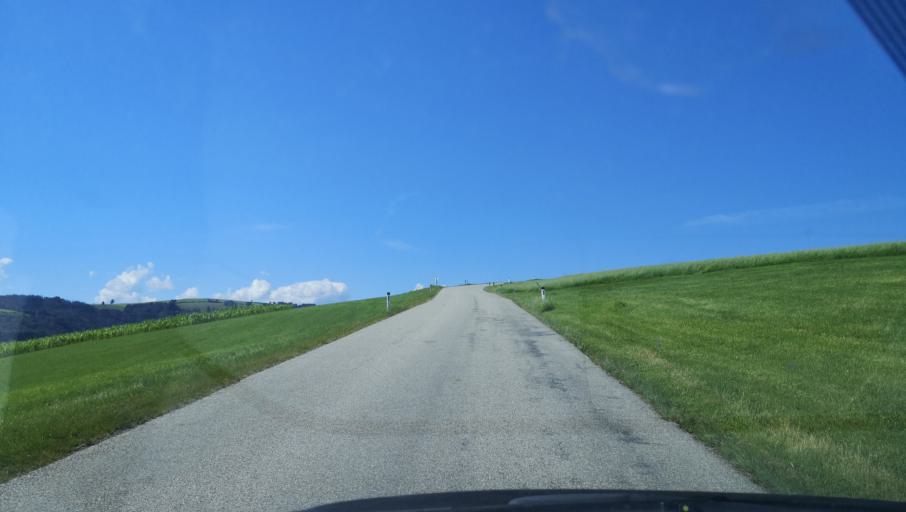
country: AT
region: Lower Austria
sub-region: Politischer Bezirk Amstetten
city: Euratsfeld
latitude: 48.0553
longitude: 14.9193
